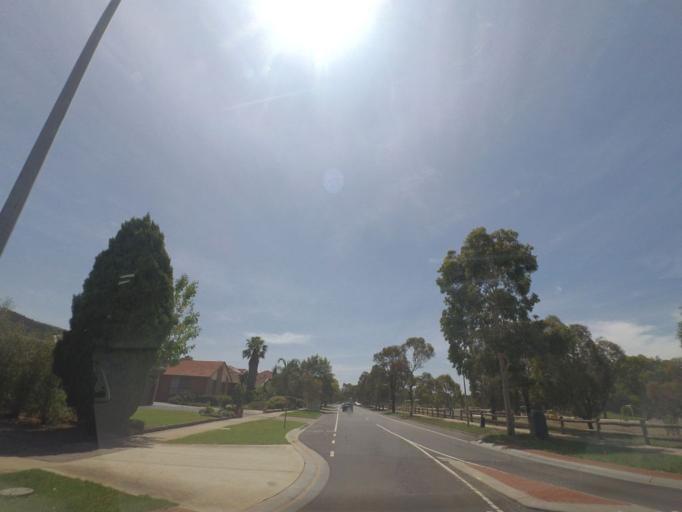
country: AU
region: Victoria
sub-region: Brimbank
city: Keilor Lodge
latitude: -37.7048
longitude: 144.7944
